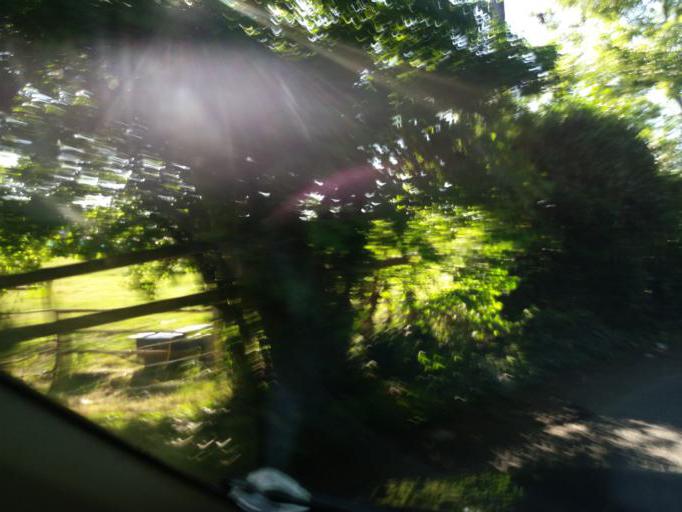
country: IE
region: Leinster
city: Ballymun
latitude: 53.4474
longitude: -6.2940
